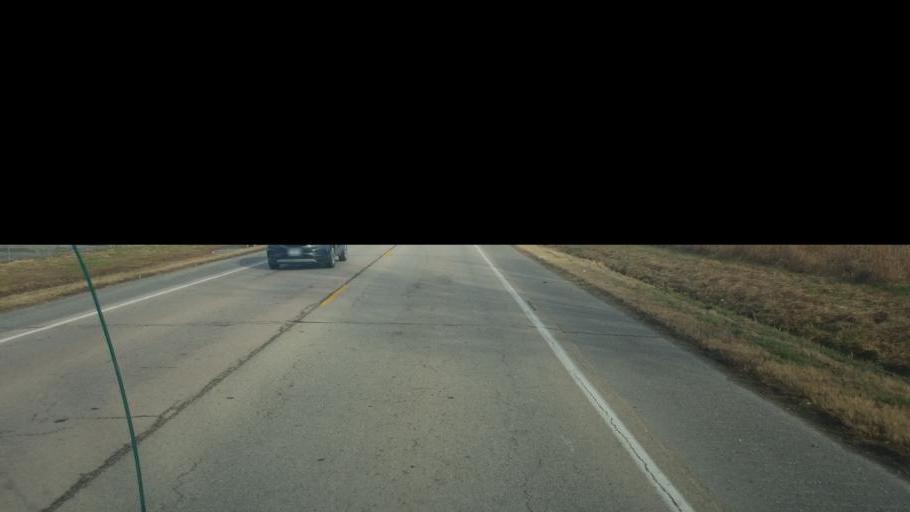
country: US
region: Missouri
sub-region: Stoddard County
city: Bloomfield
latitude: 36.8941
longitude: -89.9232
